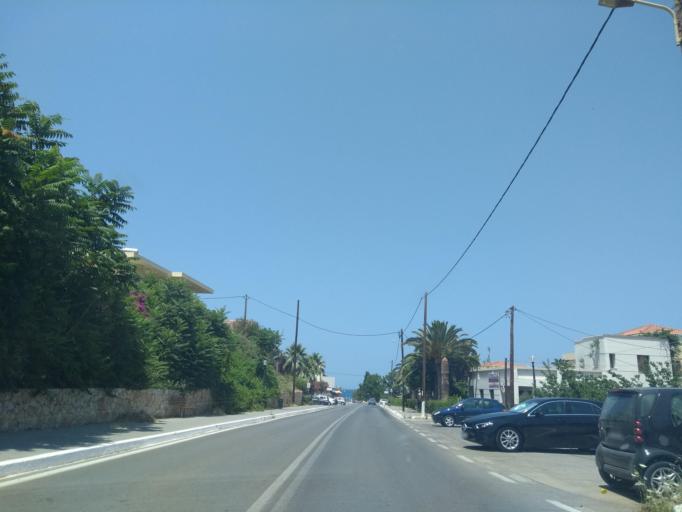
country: GR
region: Crete
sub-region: Nomos Chanias
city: Daratsos
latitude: 35.5086
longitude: 23.9883
